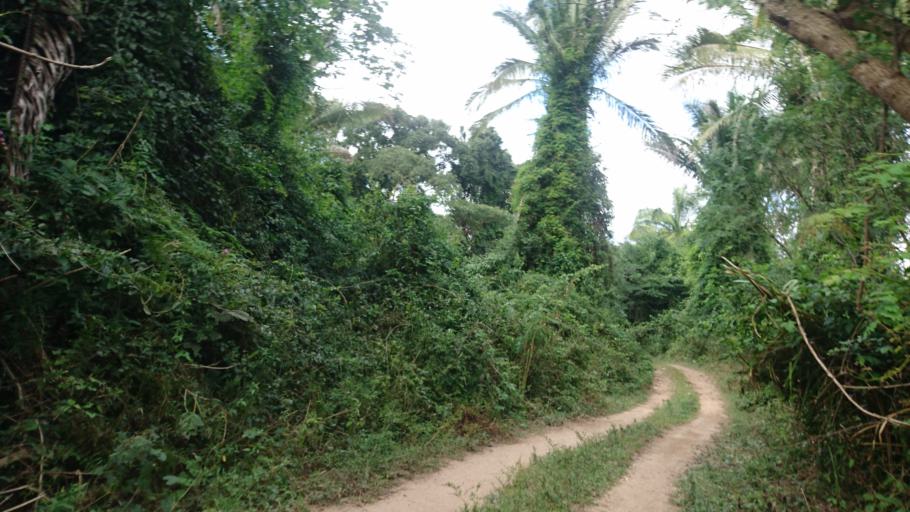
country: MX
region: Nayarit
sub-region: Bahia de Banderas
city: Corral del Risco (Punta de Mita)
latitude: 20.8311
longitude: -105.4577
